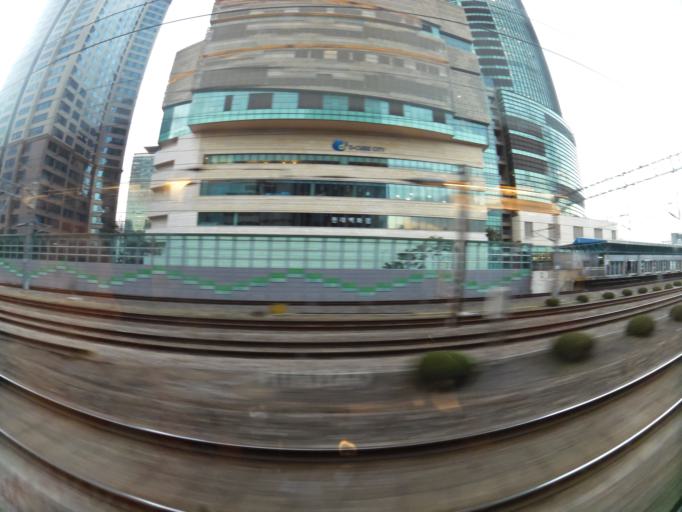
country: KR
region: Gyeonggi-do
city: Kwangmyong
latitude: 37.5079
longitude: 126.8895
